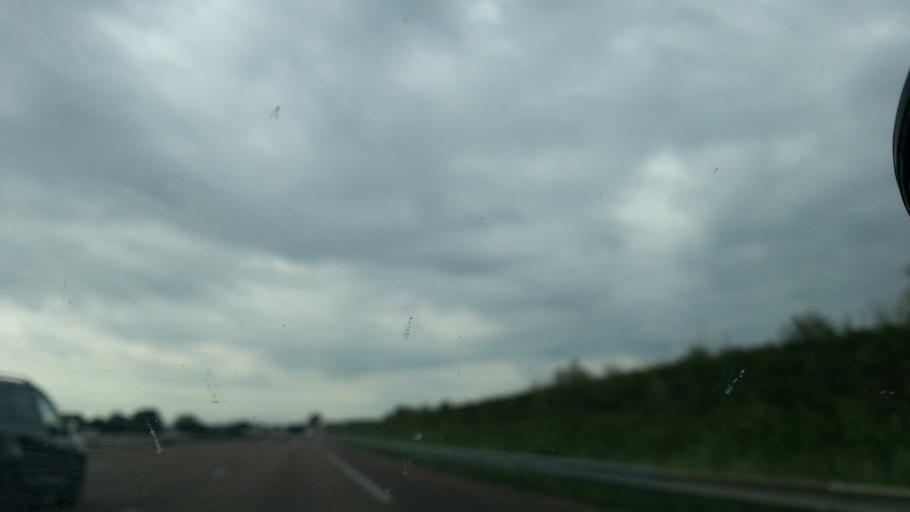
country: FR
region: Bourgogne
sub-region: Departement de Saone-et-Loire
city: Champforgeuil
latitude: 46.8468
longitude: 4.8298
